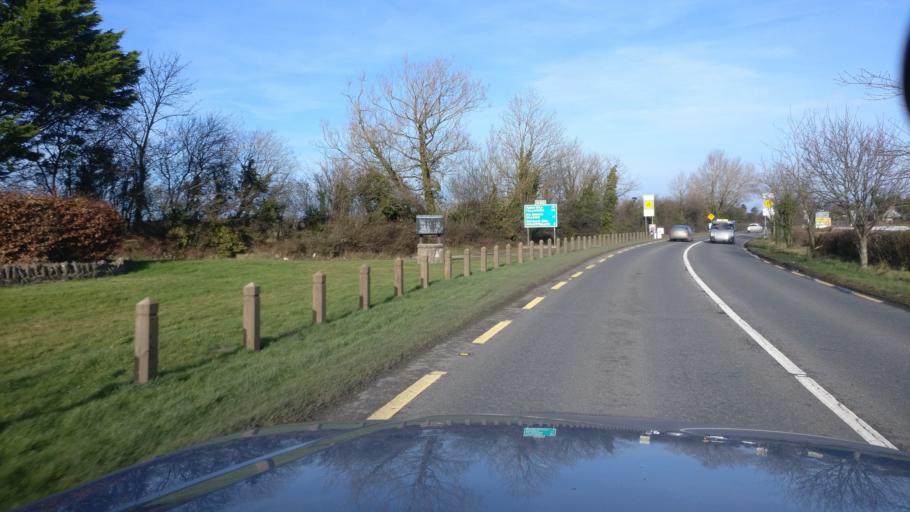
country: IE
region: Leinster
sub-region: Laois
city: Mountmellick
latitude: 53.1021
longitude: -7.3381
